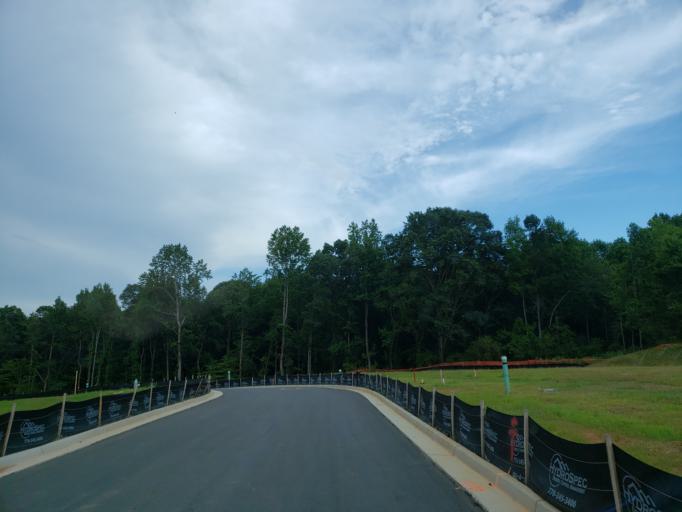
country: US
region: Georgia
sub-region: Cherokee County
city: Ball Ground
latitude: 34.2411
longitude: -84.3499
